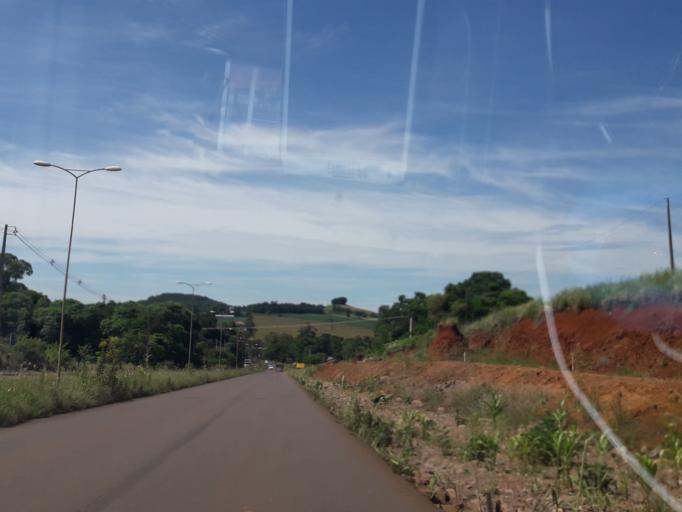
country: AR
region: Misiones
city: Bernardo de Irigoyen
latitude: -26.4431
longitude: -53.5151
